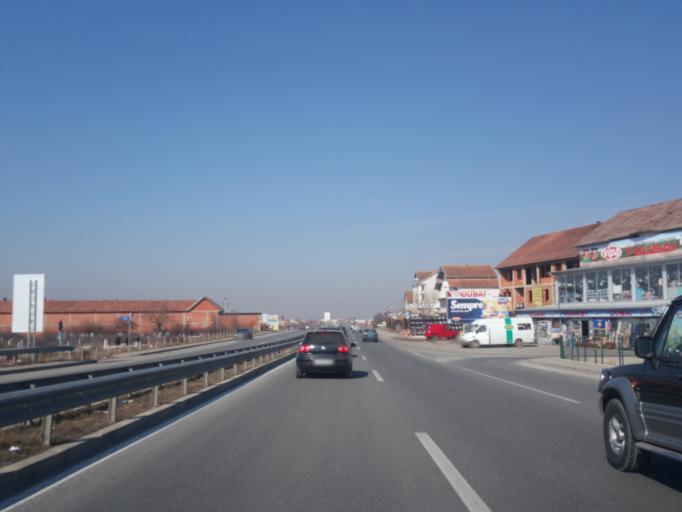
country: XK
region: Pristina
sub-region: Komuna e Obiliqit
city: Obiliq
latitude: 42.7529
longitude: 21.0390
